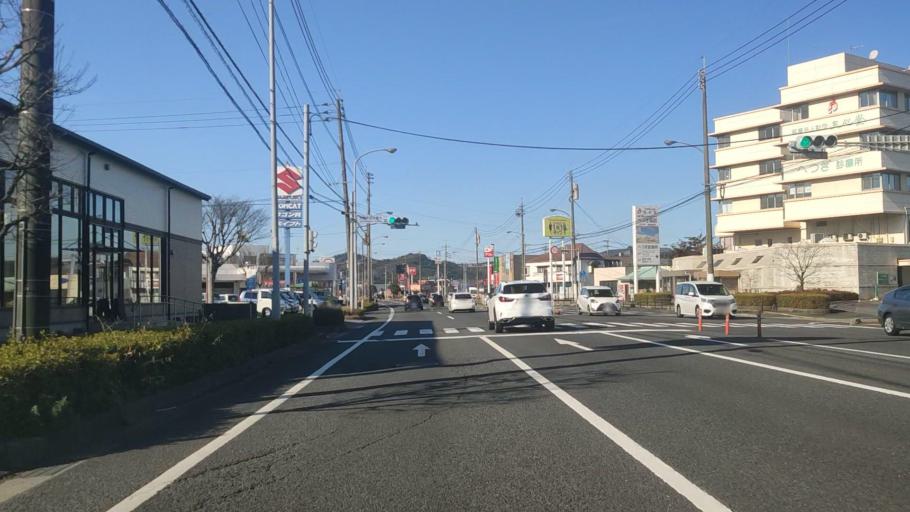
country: JP
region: Oita
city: Oita
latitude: 33.1537
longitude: 131.6558
